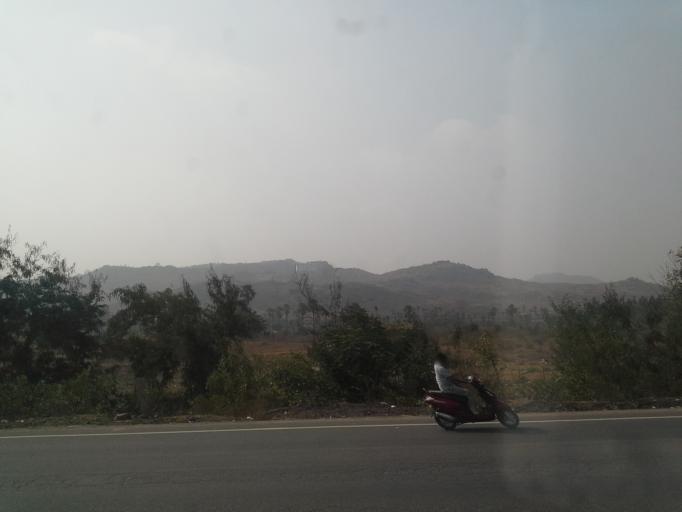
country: IN
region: Telangana
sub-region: Rangareddi
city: Lal Bahadur Nagar
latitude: 17.3146
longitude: 78.6752
